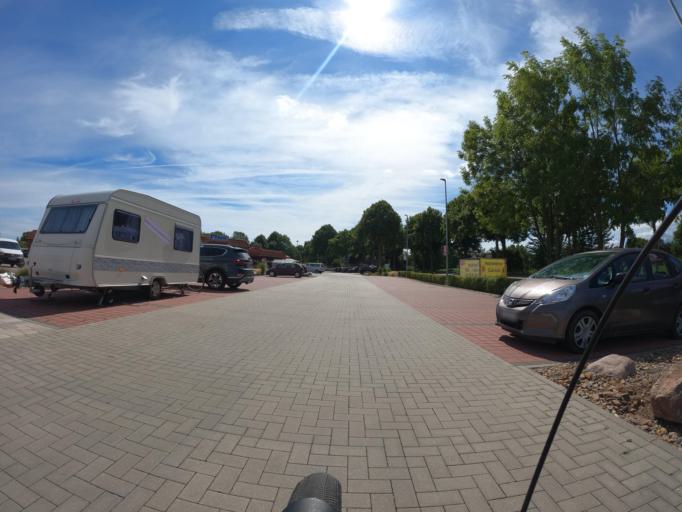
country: DE
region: Schleswig-Holstein
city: Steinbergkirche
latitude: 54.7558
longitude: 9.7565
